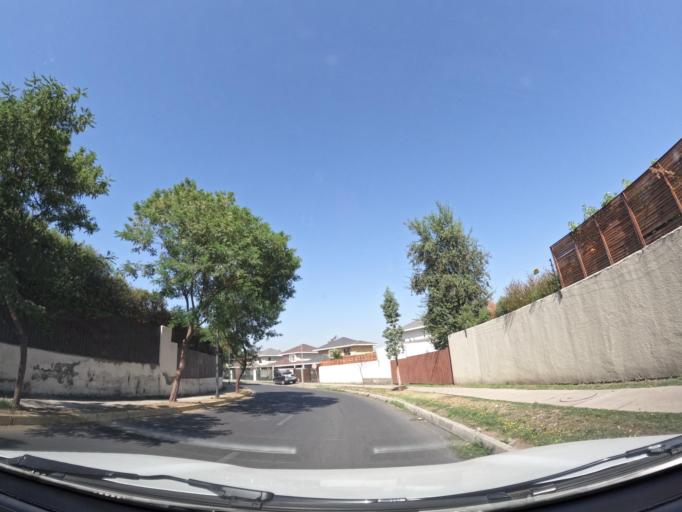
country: CL
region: Santiago Metropolitan
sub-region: Provincia de Santiago
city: Villa Presidente Frei, Nunoa, Santiago, Chile
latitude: -33.4980
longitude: -70.5550
